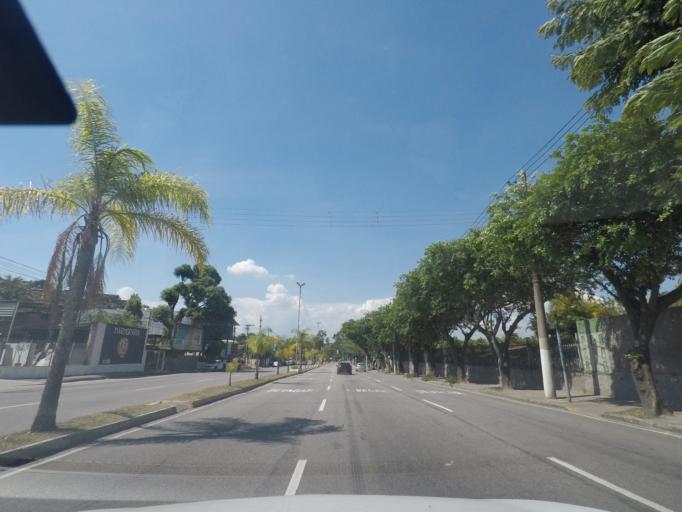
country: BR
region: Rio de Janeiro
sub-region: Niteroi
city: Niteroi
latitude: -22.9146
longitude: -43.0481
